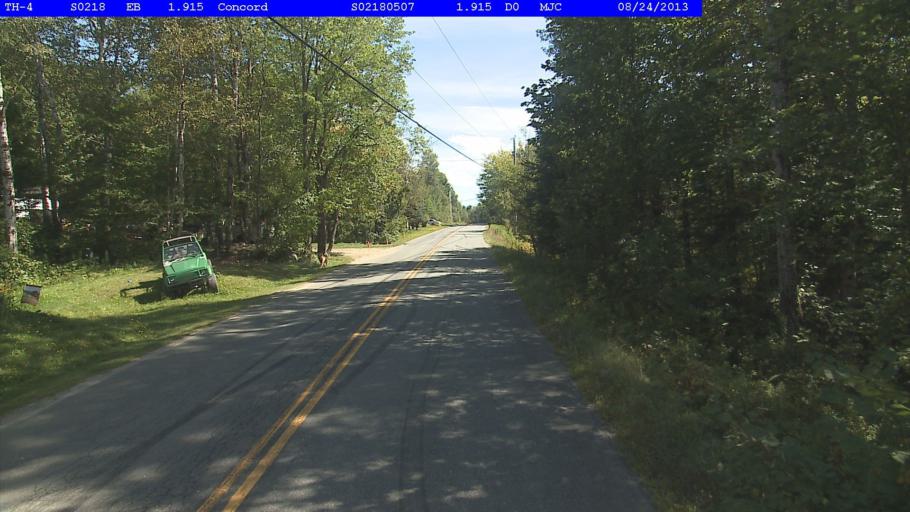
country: US
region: New Hampshire
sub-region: Grafton County
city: Littleton
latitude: 44.4398
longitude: -71.7607
